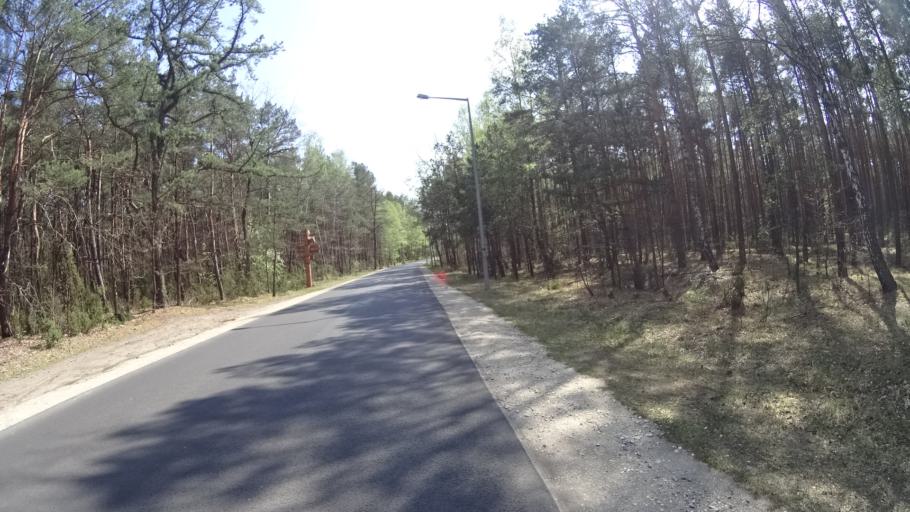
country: PL
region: Masovian Voivodeship
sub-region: Powiat warszawski zachodni
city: Izabelin
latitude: 52.3079
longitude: 20.8108
